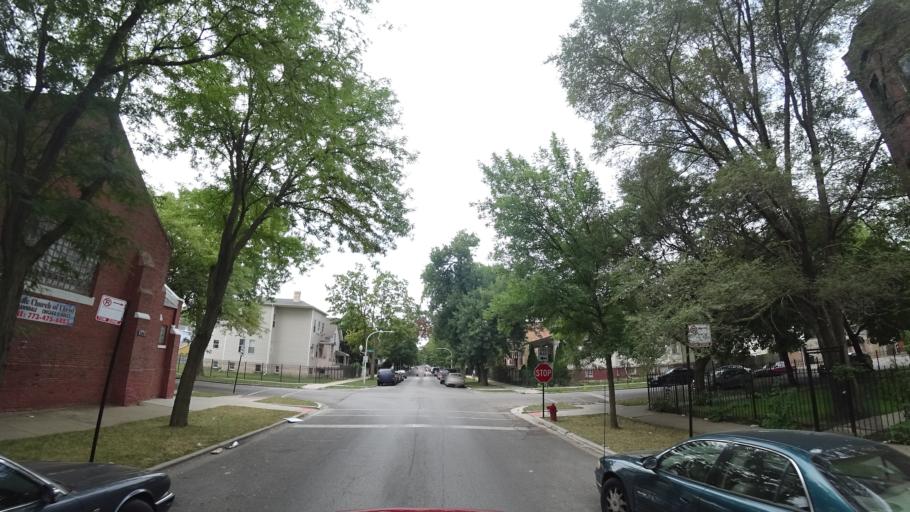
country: US
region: Illinois
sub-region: Cook County
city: Cicero
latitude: 41.8483
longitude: -87.7174
